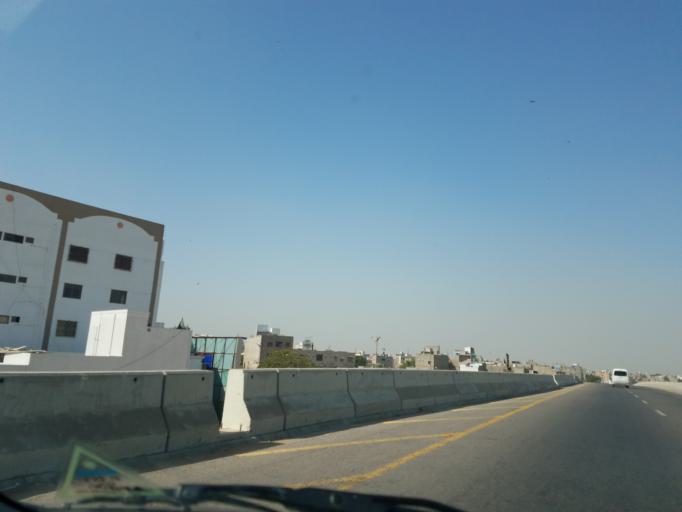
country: PK
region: Sindh
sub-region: Karachi District
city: Karachi
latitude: 24.9162
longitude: 67.0783
